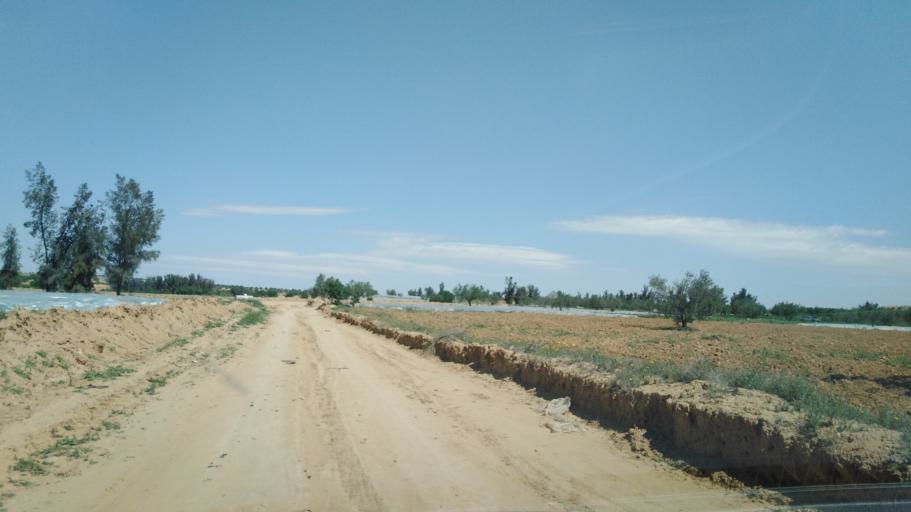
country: TN
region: Safaqis
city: Sfax
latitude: 34.7671
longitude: 10.5277
